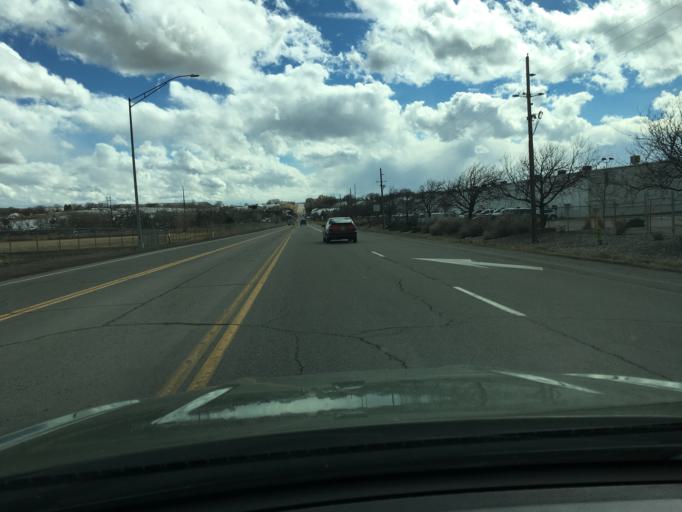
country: US
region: Colorado
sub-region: Mesa County
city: Clifton
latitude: 39.0617
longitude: -108.4595
